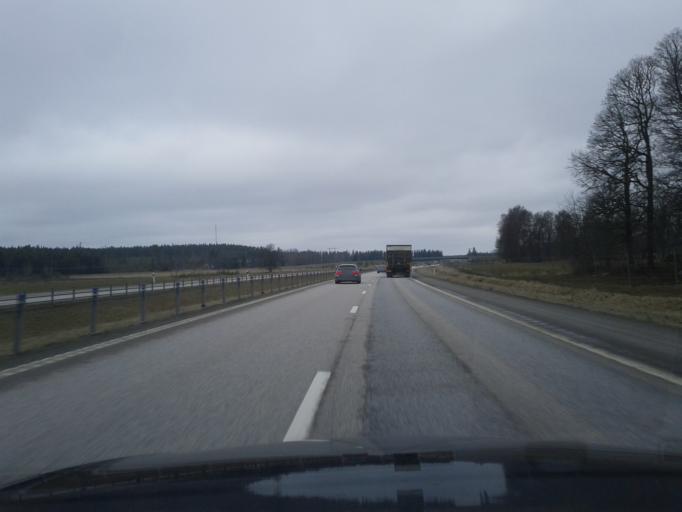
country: SE
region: Uppsala
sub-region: Osthammars Kommun
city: Bjorklinge
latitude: 60.0968
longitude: 17.5691
